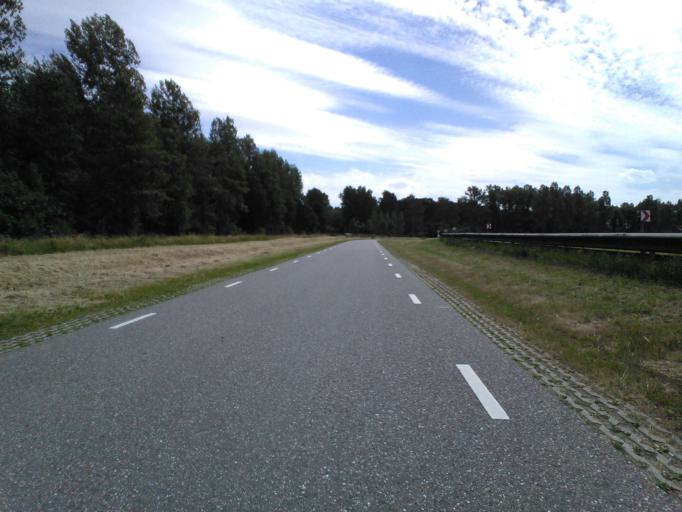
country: NL
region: South Holland
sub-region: Gemeente Papendrecht
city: Papendrecht
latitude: 51.8477
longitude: 4.7322
